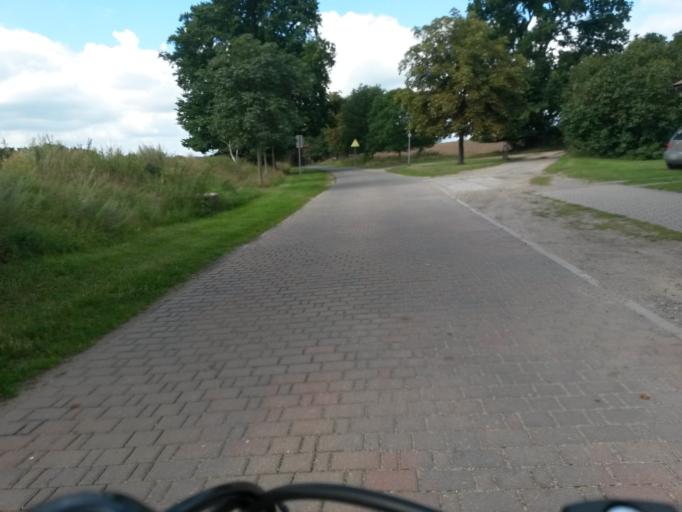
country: DE
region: Brandenburg
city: Althuttendorf
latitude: 53.0256
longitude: 13.8922
